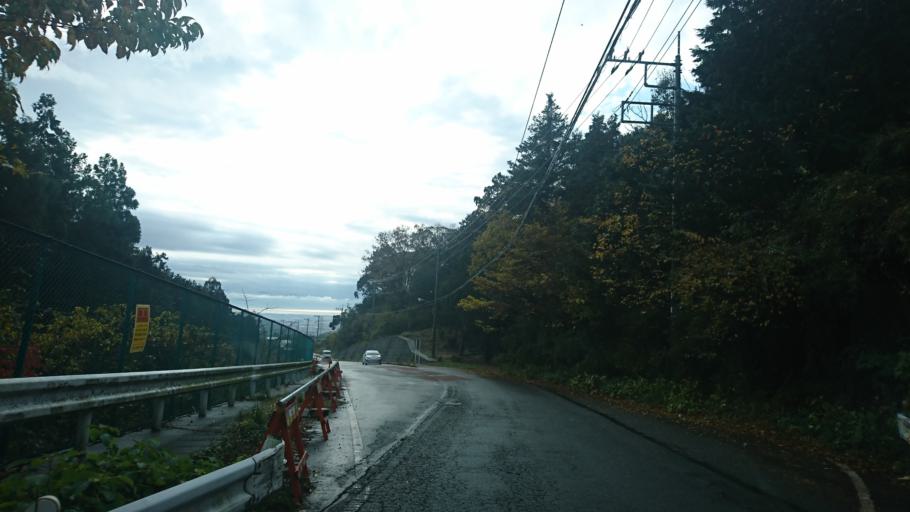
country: JP
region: Shizuoka
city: Fuji
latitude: 35.1791
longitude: 138.7263
